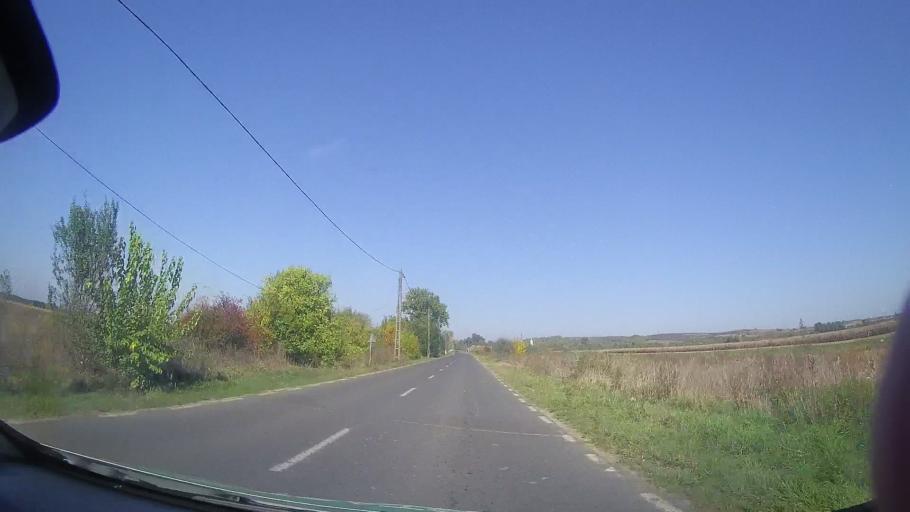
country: RO
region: Timis
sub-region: Comuna Balint
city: Balint
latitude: 45.8053
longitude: 21.8612
